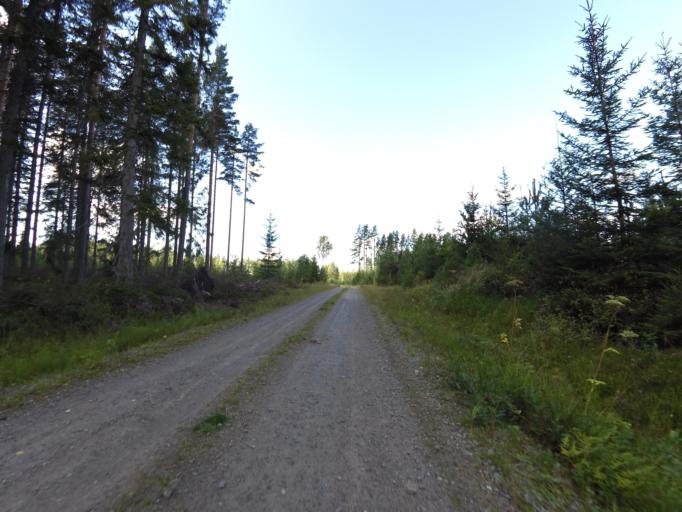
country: SE
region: Gaevleborg
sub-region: Ockelbo Kommun
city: Ockelbo
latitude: 60.8126
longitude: 16.7655
